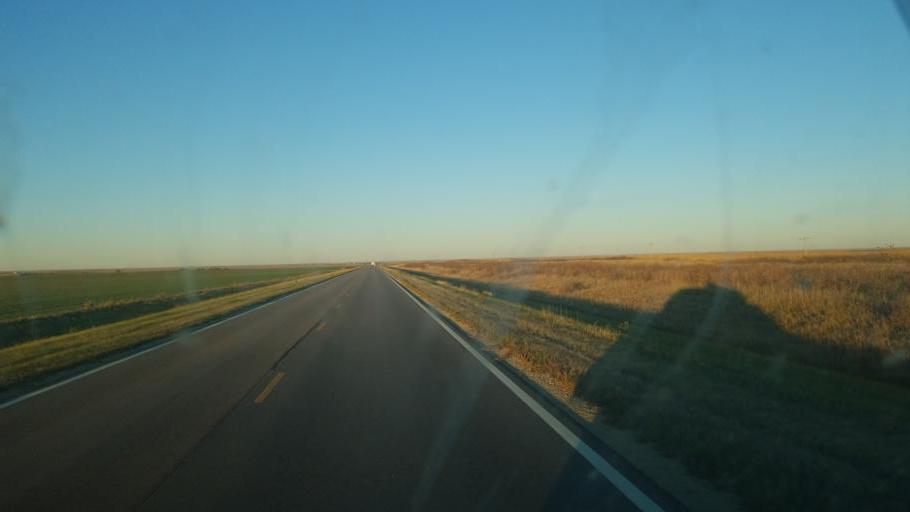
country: US
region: Kansas
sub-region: Wallace County
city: Sharon Springs
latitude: 38.8663
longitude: -101.9836
